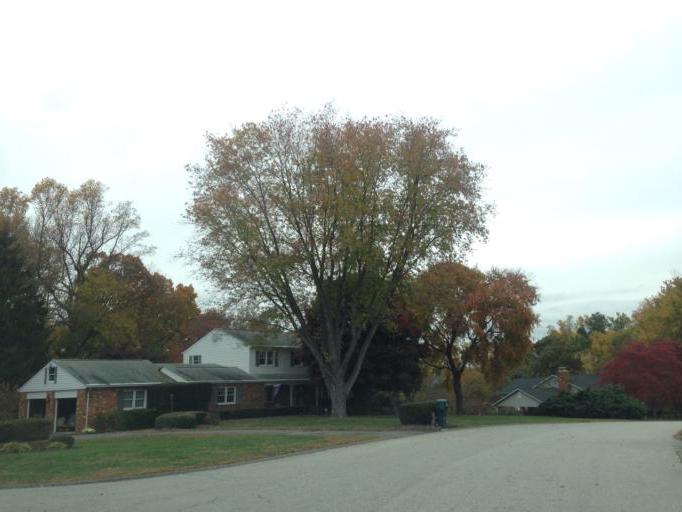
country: US
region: Maryland
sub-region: Howard County
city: Ellicott City
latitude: 39.3048
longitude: -76.8379
